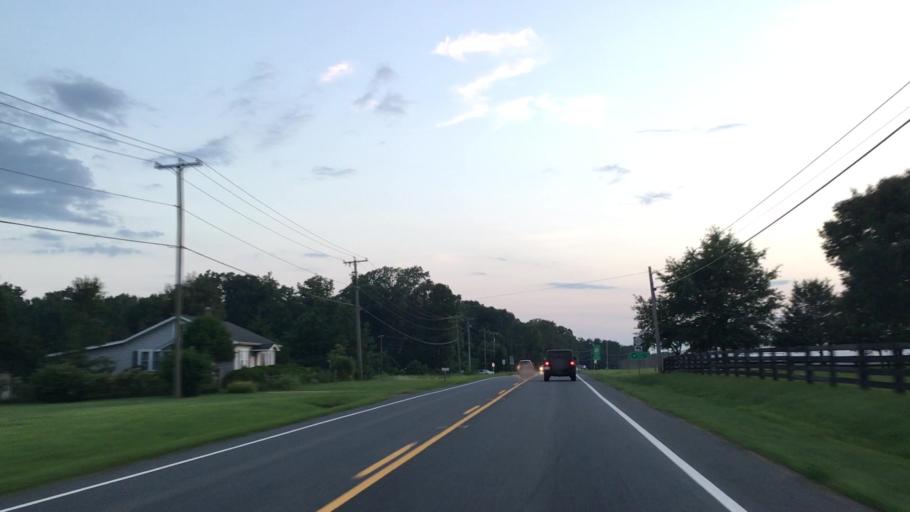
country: US
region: Virginia
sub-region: Orange County
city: Orange
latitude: 38.2498
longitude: -78.0358
